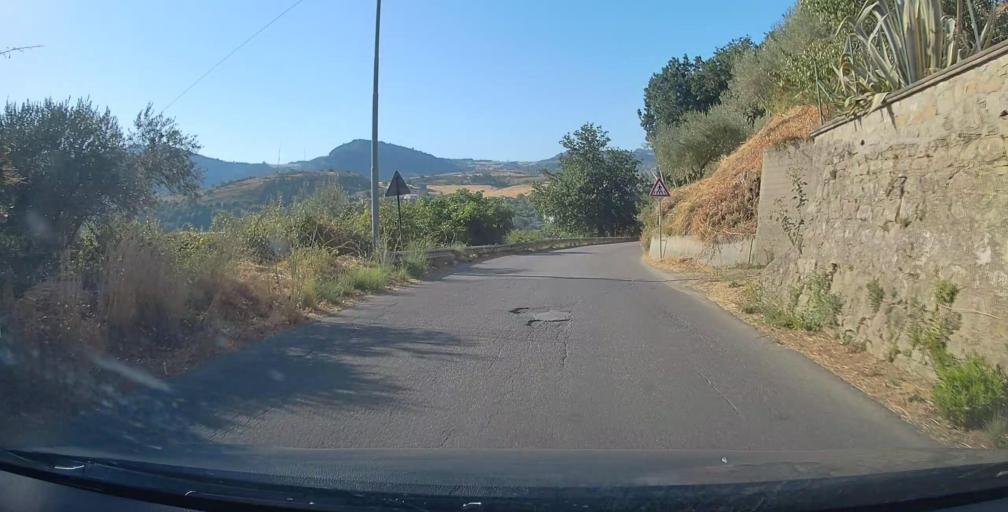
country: IT
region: Sicily
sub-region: Messina
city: Librizzi
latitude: 38.0820
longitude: 14.9745
